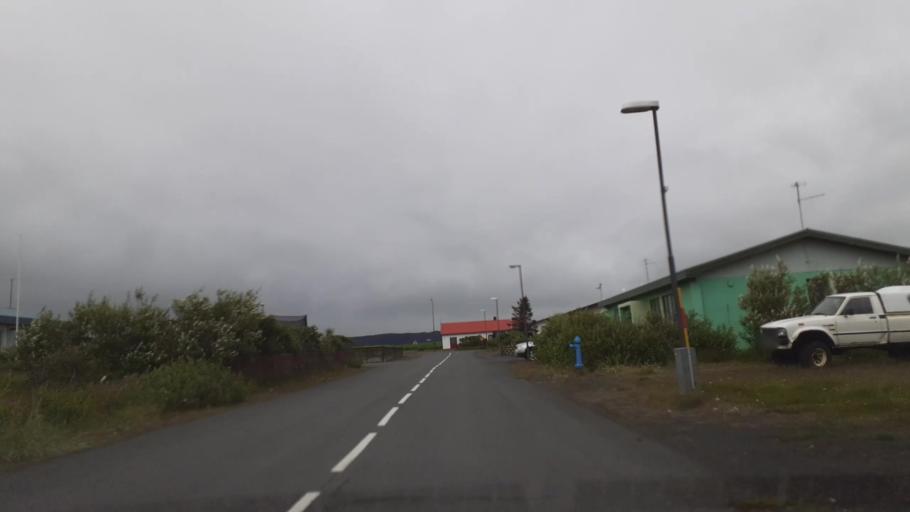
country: IS
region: Northeast
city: Husavik
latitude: 66.3030
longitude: -16.4470
